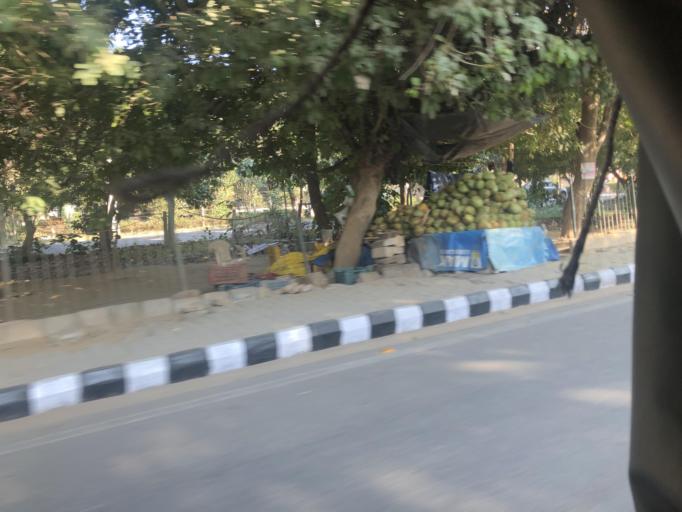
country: IN
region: Haryana
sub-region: Gurgaon
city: Gurgaon
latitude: 28.4523
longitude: 77.0758
